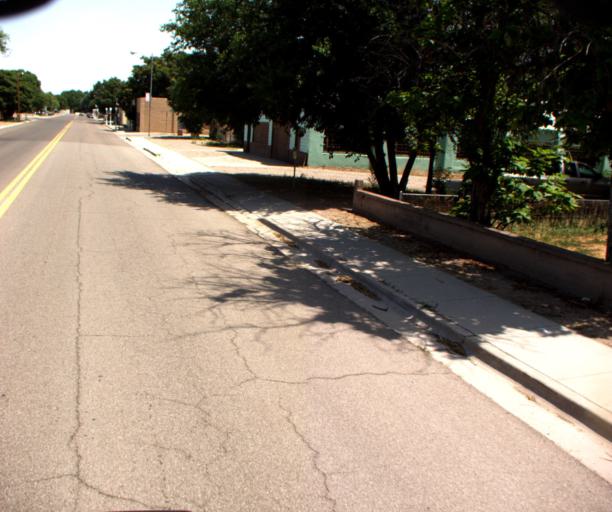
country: US
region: Arizona
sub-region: Greenlee County
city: Clifton
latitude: 32.7229
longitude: -109.1058
